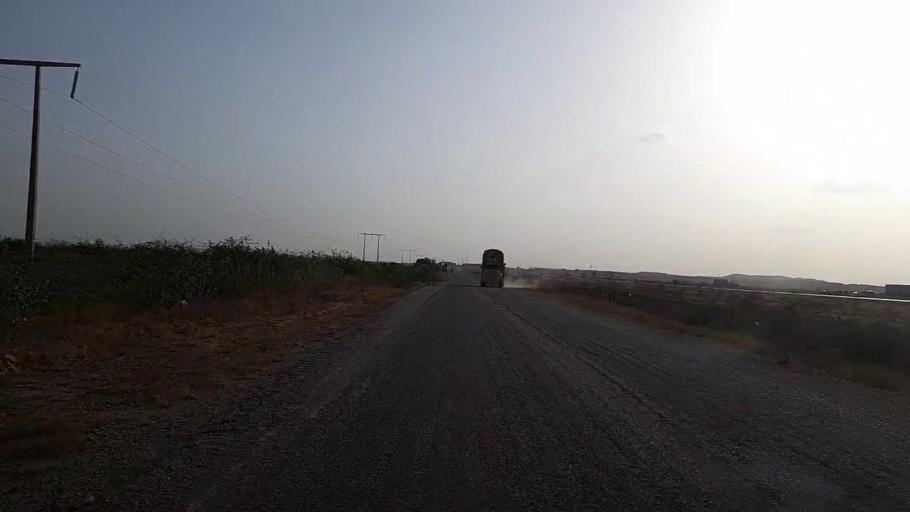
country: PK
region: Sindh
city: Thatta
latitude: 25.1889
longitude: 67.8444
